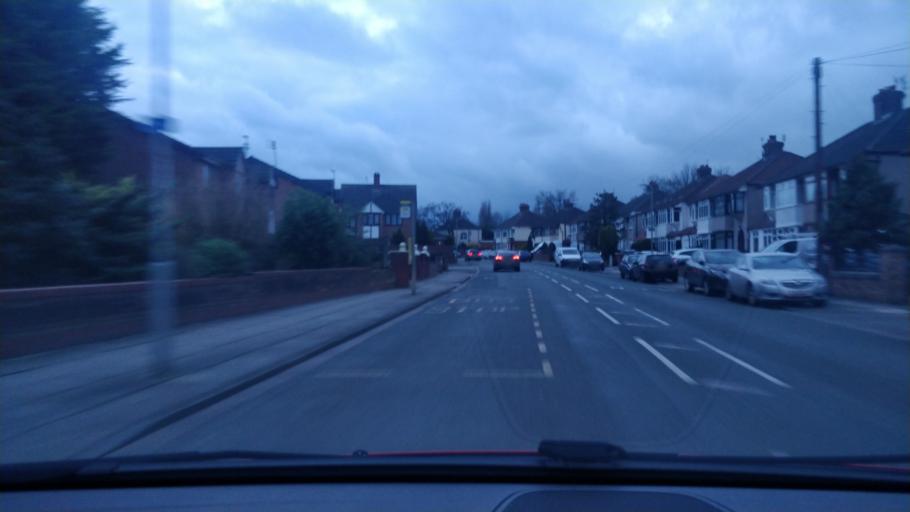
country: GB
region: England
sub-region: Knowsley
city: Knowsley
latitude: 53.4282
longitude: -2.8850
